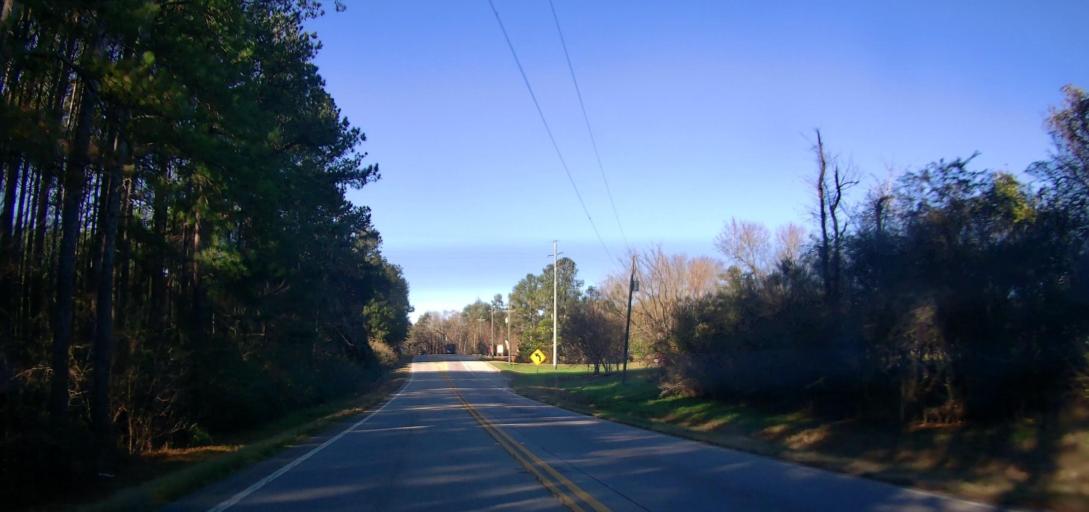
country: US
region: Georgia
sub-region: Hall County
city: Lula
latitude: 34.4025
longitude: -83.6980
